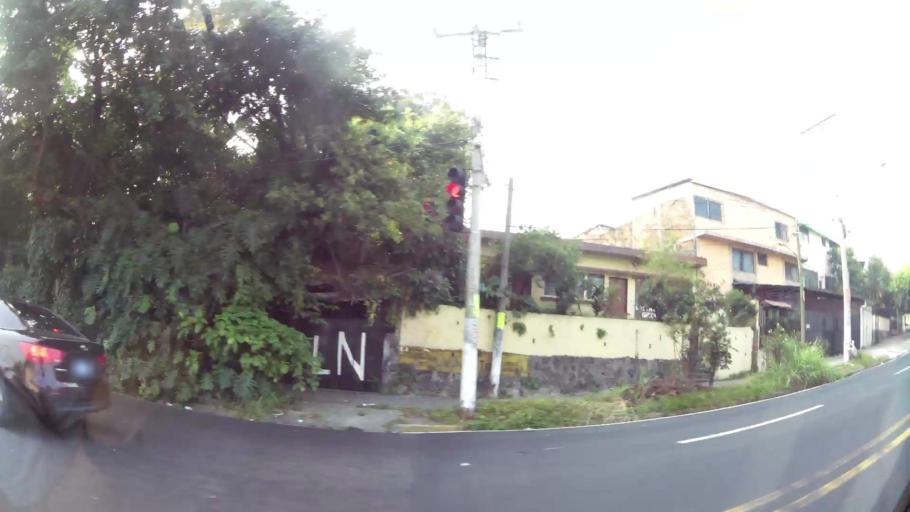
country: SV
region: San Salvador
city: San Salvador
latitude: 13.6879
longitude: -89.2062
